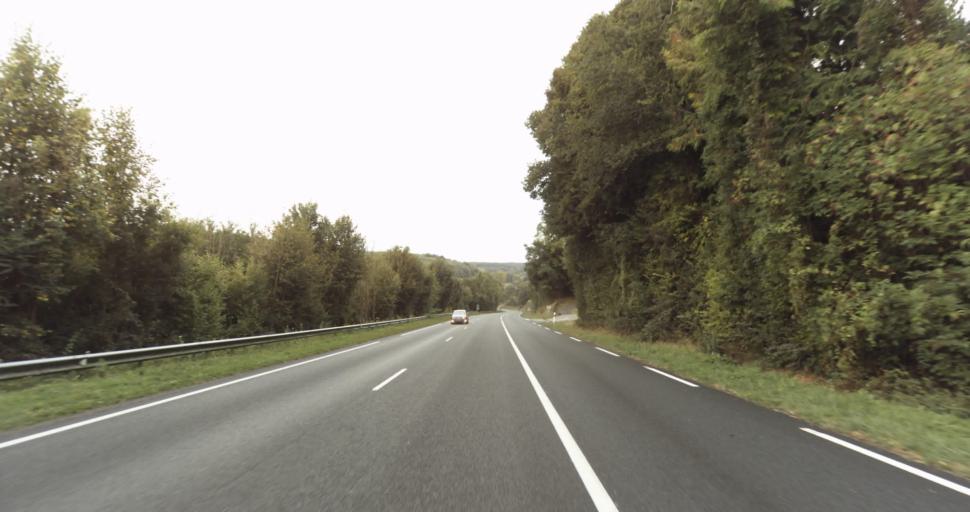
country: FR
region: Lower Normandy
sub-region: Departement de l'Orne
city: Gace
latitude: 48.8438
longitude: 0.2653
